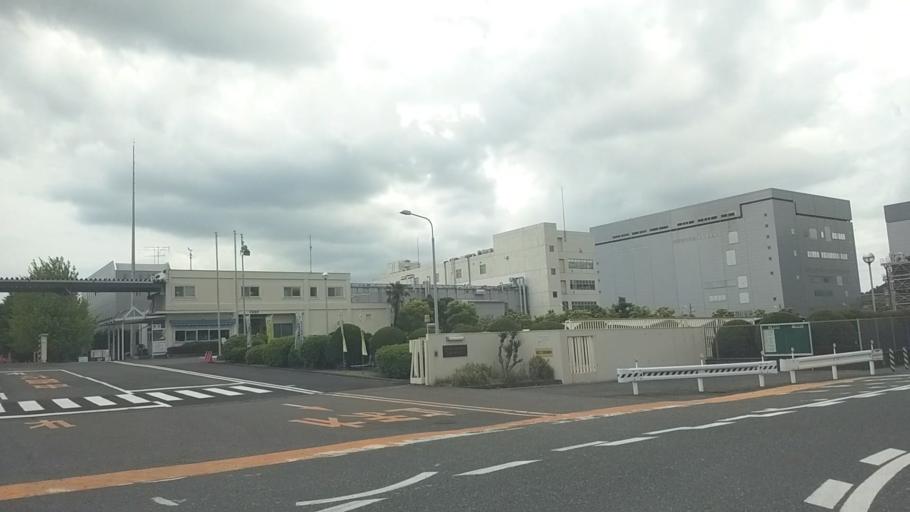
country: JP
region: Kanagawa
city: Fujisawa
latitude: 35.3714
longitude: 139.5246
